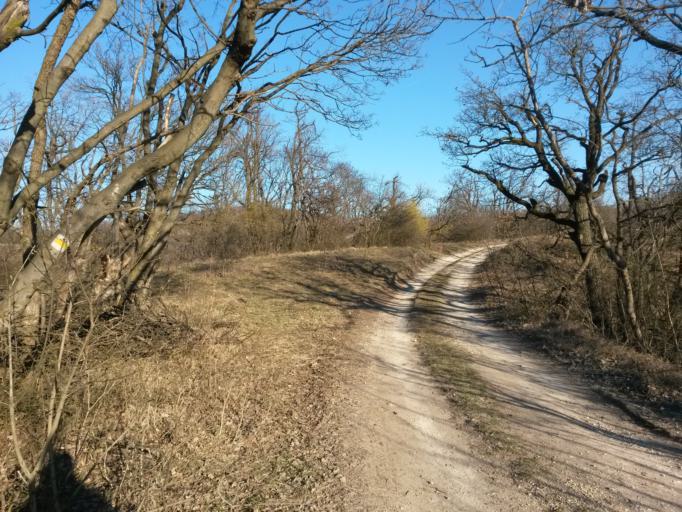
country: HU
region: Pest
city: Telki
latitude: 47.5886
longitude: 18.8368
